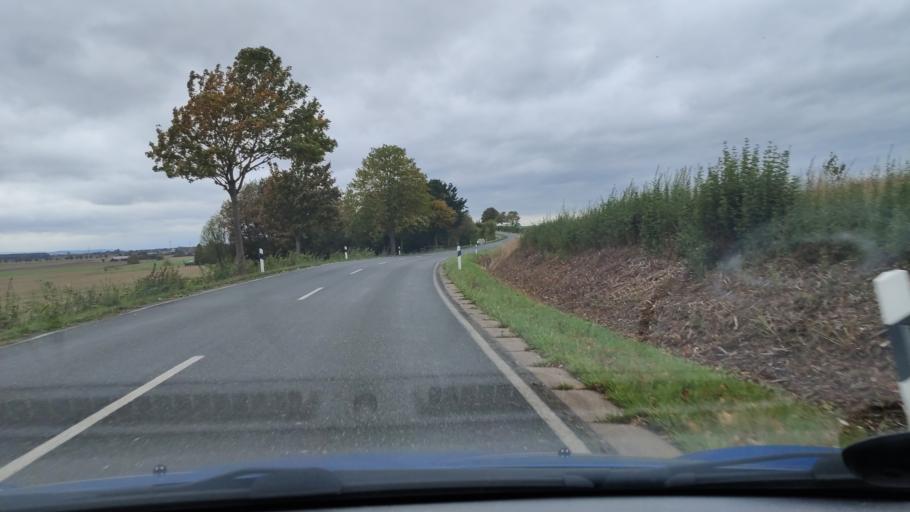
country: DE
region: Lower Saxony
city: Seelze
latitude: 52.3776
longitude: 9.6443
